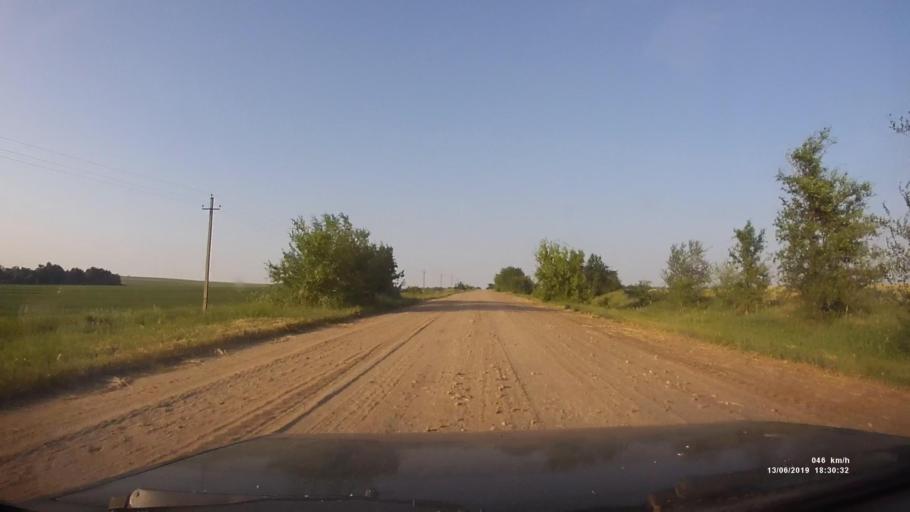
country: RU
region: Rostov
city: Kazanskaya
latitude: 49.8626
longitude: 41.3510
